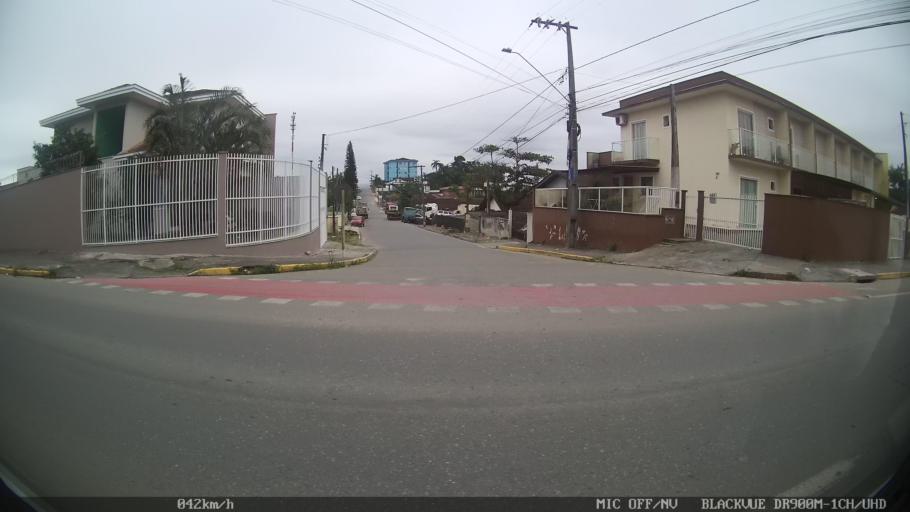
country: BR
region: Santa Catarina
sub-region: Joinville
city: Joinville
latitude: -26.2924
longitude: -48.9043
